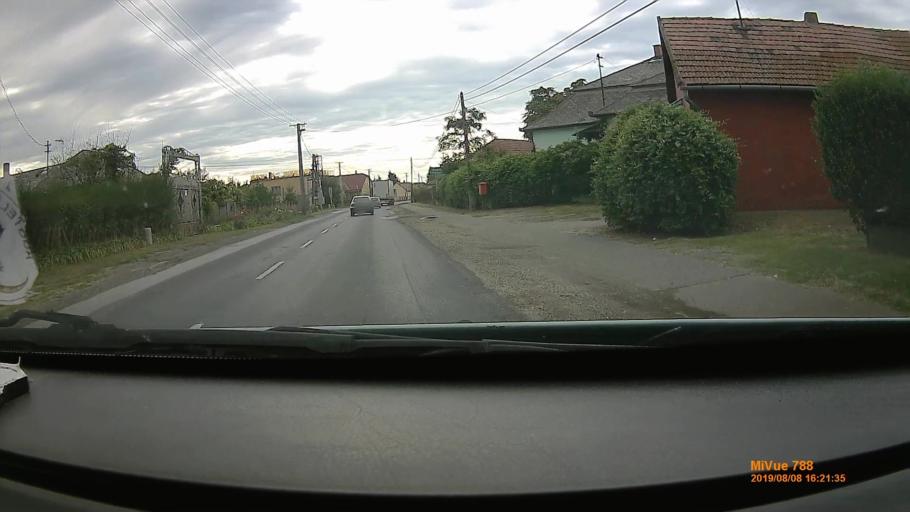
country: HU
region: Szabolcs-Szatmar-Bereg
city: Nyirmeggyes
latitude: 47.9693
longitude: 22.2574
